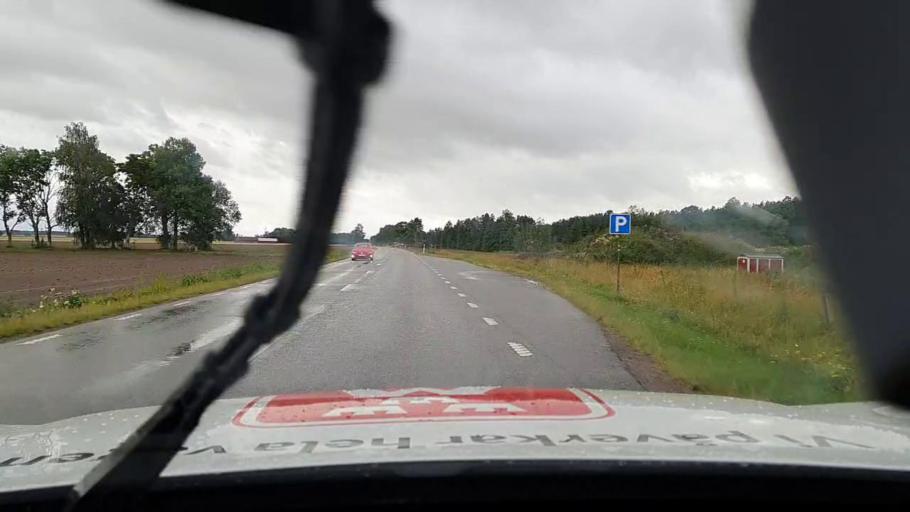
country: SE
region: Vaestra Goetaland
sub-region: Toreboda Kommun
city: Toereboda
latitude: 58.6333
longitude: 14.0218
